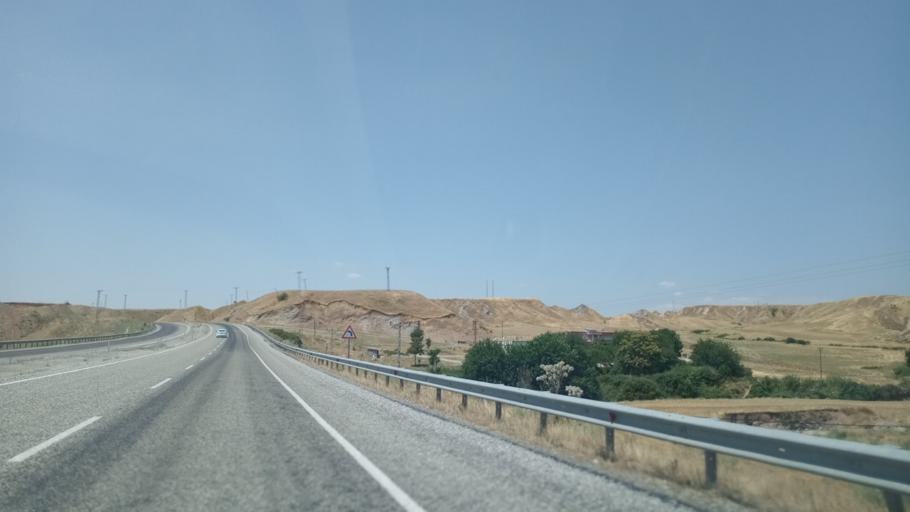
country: TR
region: Batman
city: Bekirhan
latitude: 38.1506
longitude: 41.3086
